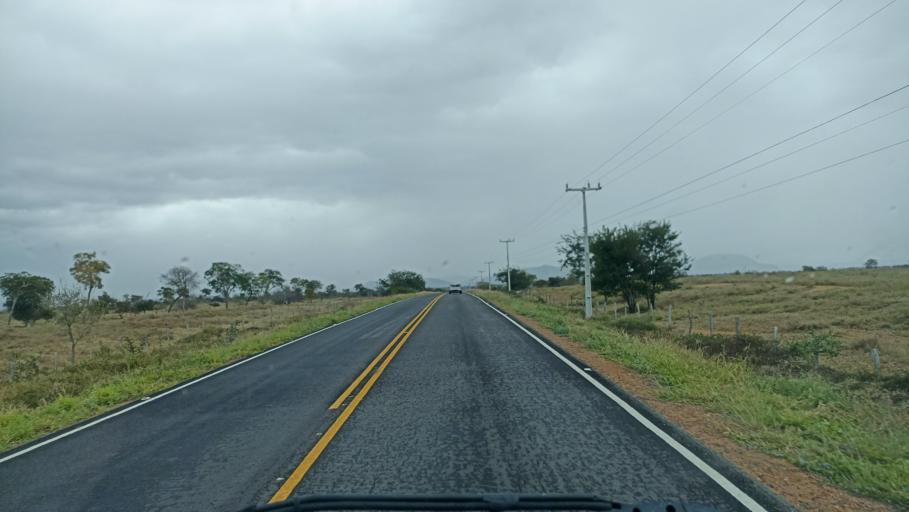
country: BR
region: Bahia
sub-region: Maracas
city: Maracas
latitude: -13.0365
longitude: -40.6937
